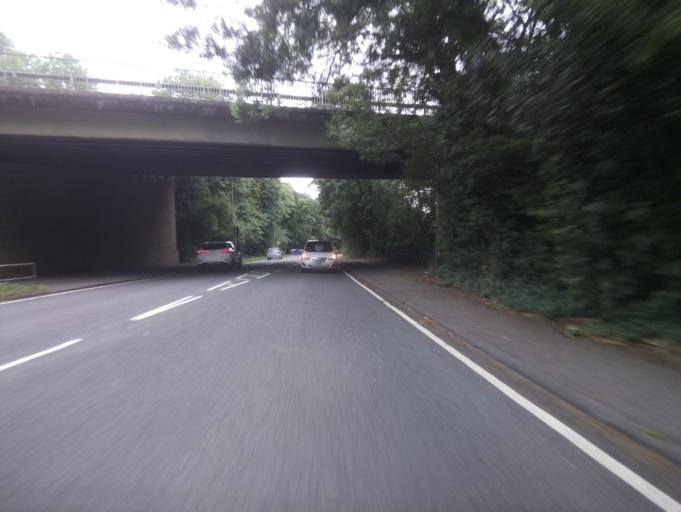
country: GB
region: England
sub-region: Worcestershire
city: Fernhill Heath
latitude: 52.2249
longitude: -2.2087
